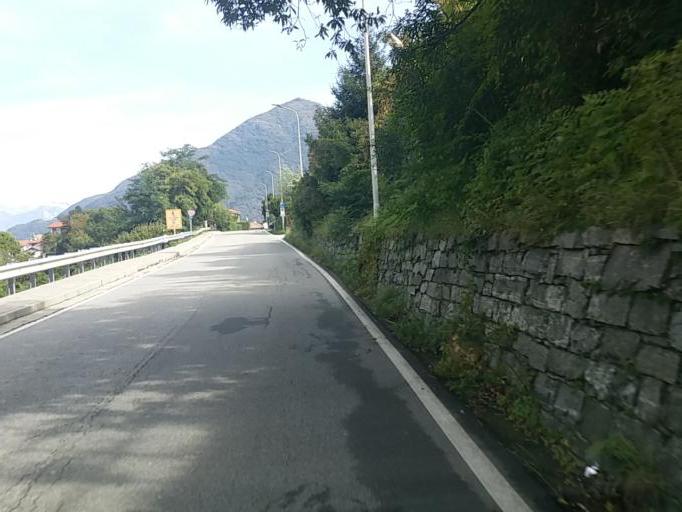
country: IT
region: Piedmont
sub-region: Provincia Verbano-Cusio-Ossola
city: Cannobio
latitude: 46.0587
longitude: 8.6916
